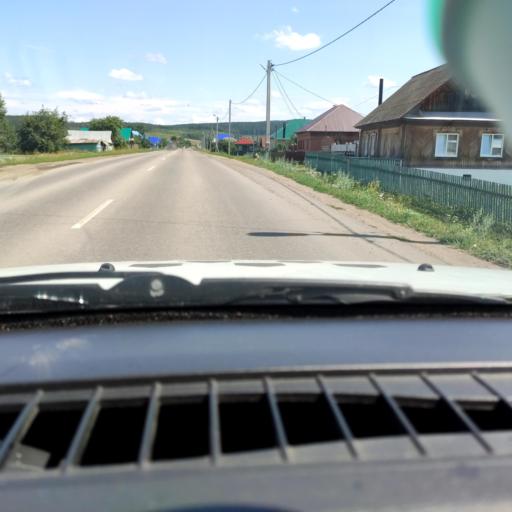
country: RU
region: Bashkortostan
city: Mesyagutovo
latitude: 55.5296
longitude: 58.2599
